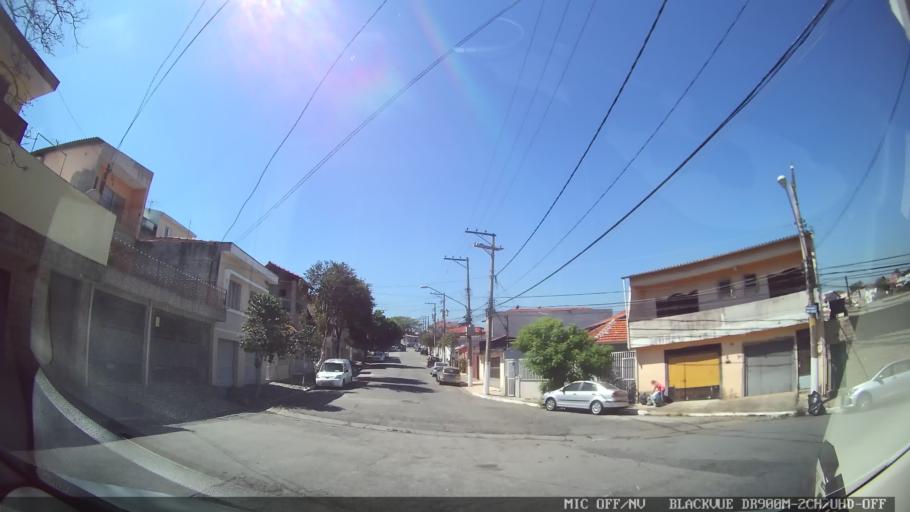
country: BR
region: Sao Paulo
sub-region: Sao Paulo
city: Sao Paulo
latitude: -23.5053
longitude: -46.6570
